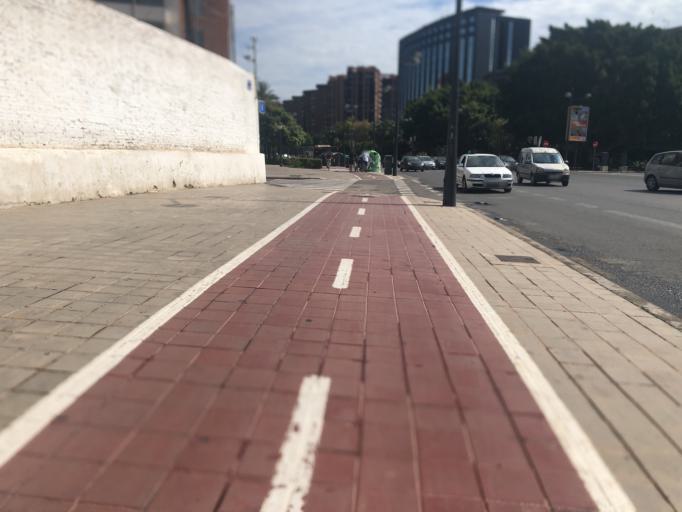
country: ES
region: Valencia
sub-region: Provincia de Valencia
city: Valencia
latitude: 39.4702
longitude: -0.3592
